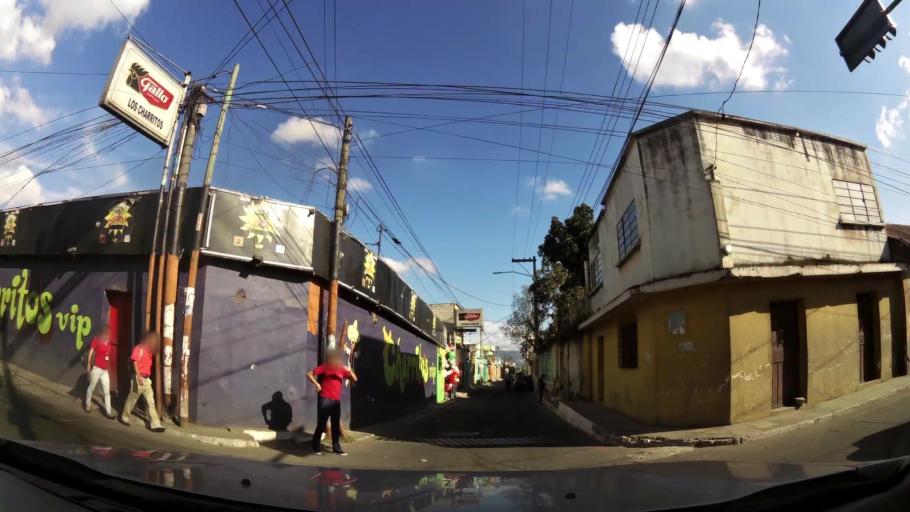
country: GT
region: Guatemala
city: Villa Nueva
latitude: 14.5275
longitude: -90.5875
